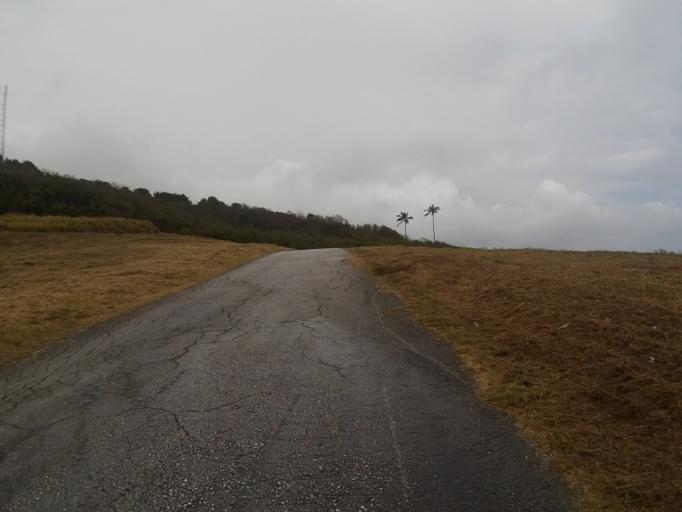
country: BB
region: Saint Andrew
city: Greenland
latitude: 13.2743
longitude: -59.5816
